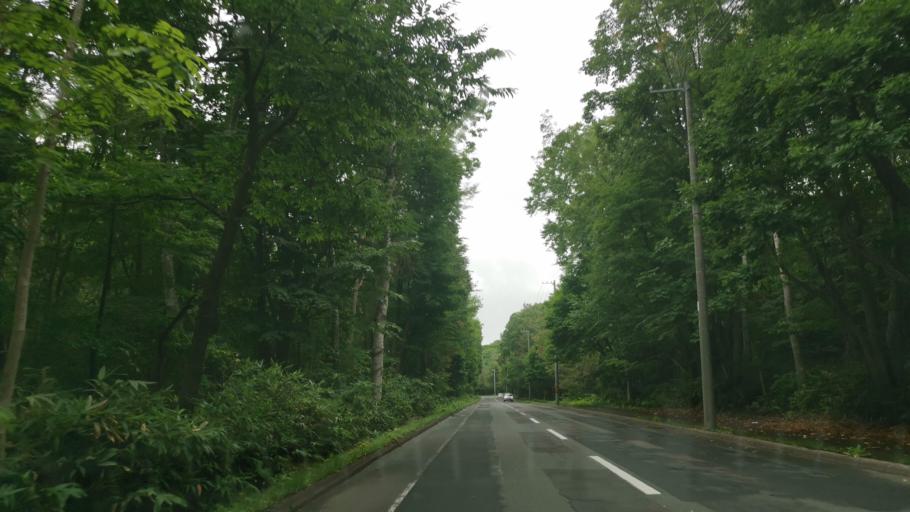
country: JP
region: Hokkaido
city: Sapporo
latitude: 42.9776
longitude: 141.3587
